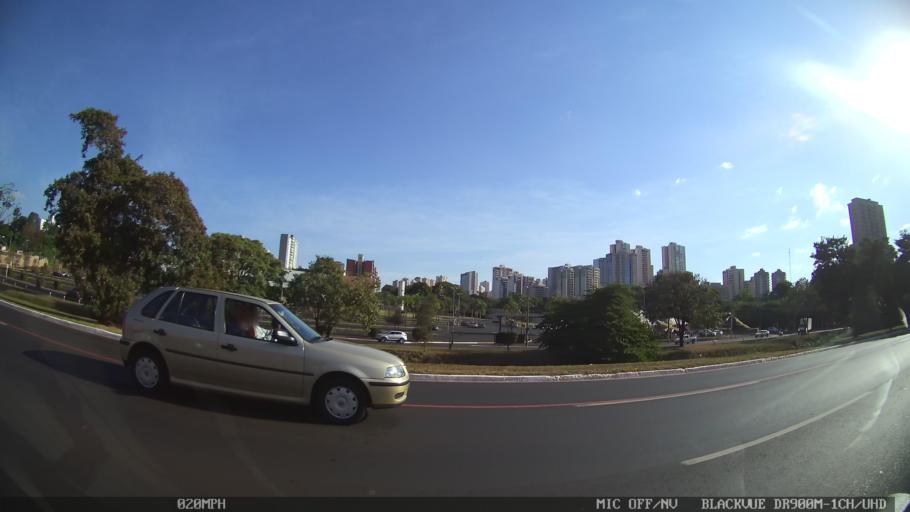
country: BR
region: Sao Paulo
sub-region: Ribeirao Preto
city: Ribeirao Preto
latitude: -21.2079
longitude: -47.7897
